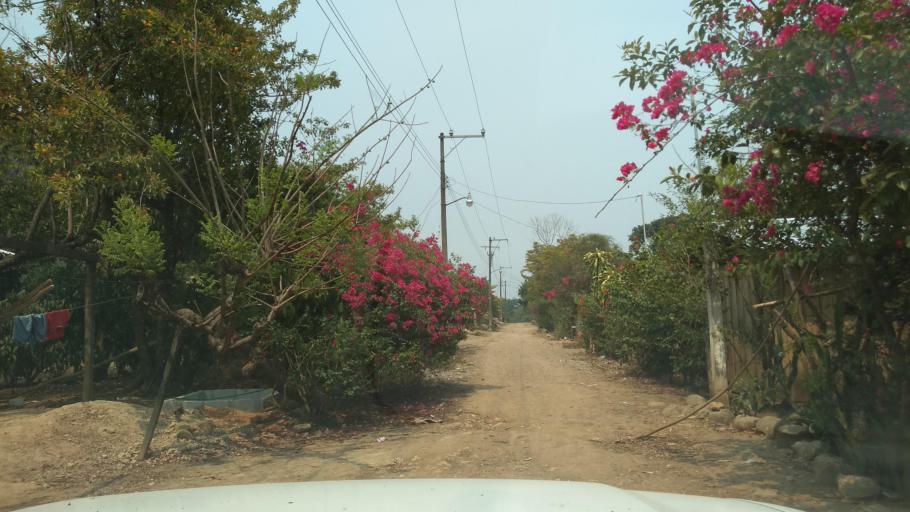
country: MX
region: Veracruz
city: Cosolapa
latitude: 18.5881
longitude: -96.7134
